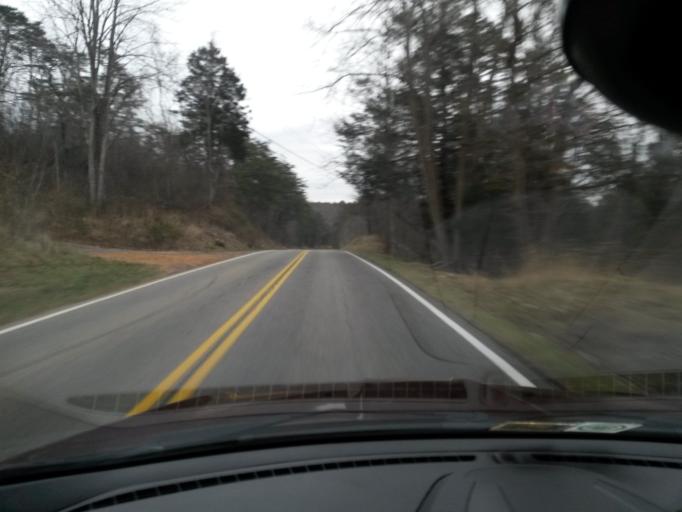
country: US
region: Virginia
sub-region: Rockbridge County
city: East Lexington
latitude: 38.0013
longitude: -79.5281
